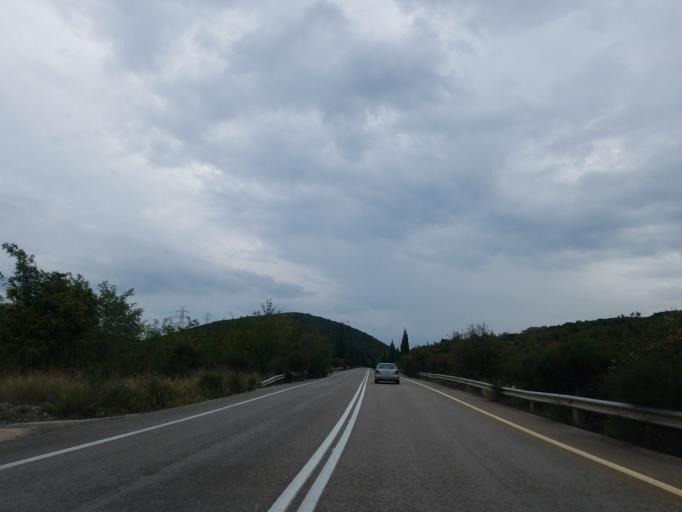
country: GR
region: Central Greece
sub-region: Nomos Voiotias
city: Livadeia
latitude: 38.4443
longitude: 22.8018
